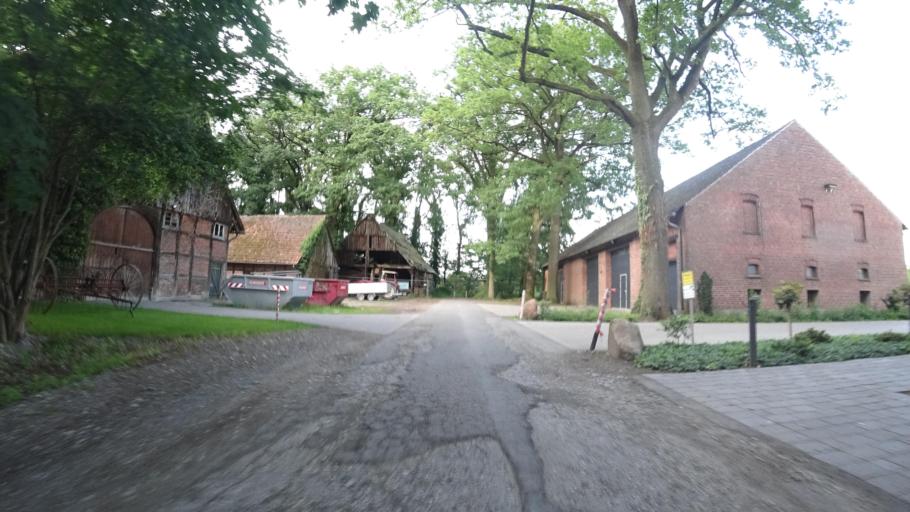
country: DE
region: North Rhine-Westphalia
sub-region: Regierungsbezirk Detmold
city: Guetersloh
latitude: 51.9123
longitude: 8.4395
